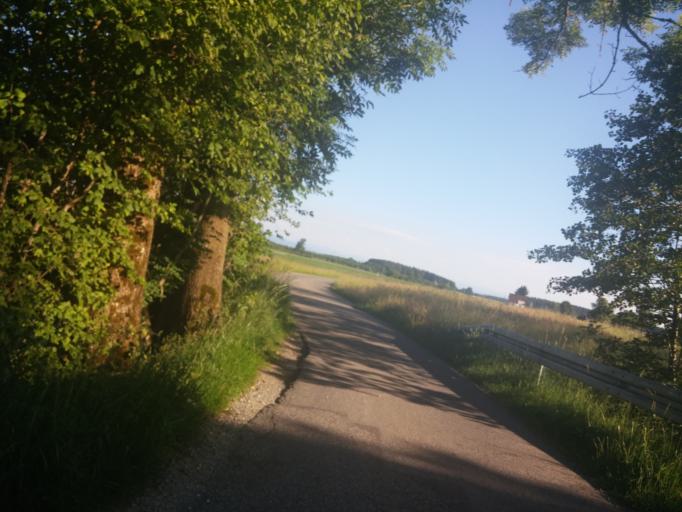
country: DE
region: Baden-Wuerttemberg
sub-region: Tuebingen Region
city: Kisslegg
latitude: 47.7790
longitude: 9.8711
